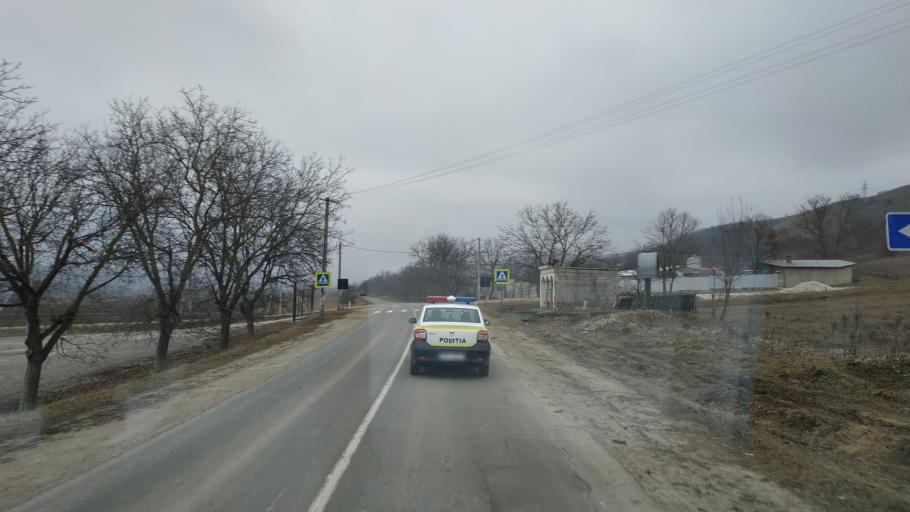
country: MD
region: Hincesti
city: Hincesti
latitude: 46.9686
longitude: 28.4771
